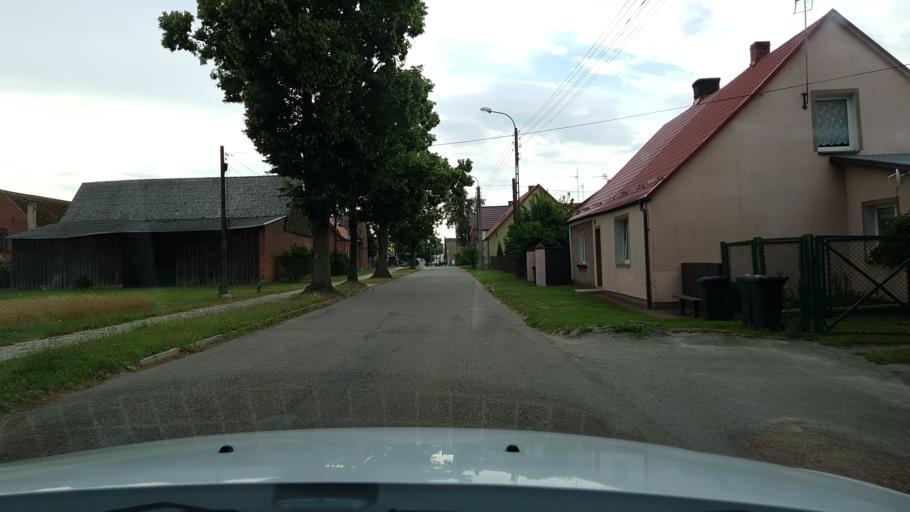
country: PL
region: West Pomeranian Voivodeship
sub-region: Powiat drawski
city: Wierzchowo
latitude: 53.4579
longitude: 16.1065
